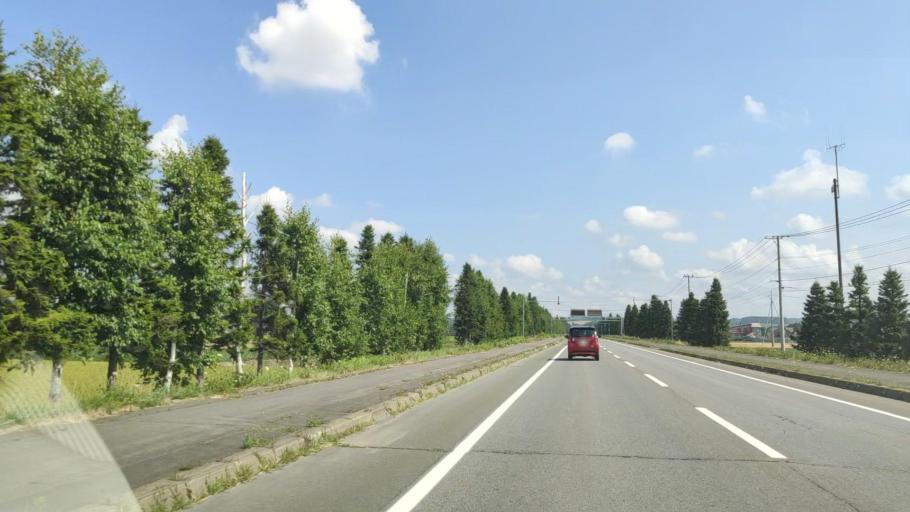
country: JP
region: Hokkaido
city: Shimo-furano
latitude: 43.4770
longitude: 142.4573
